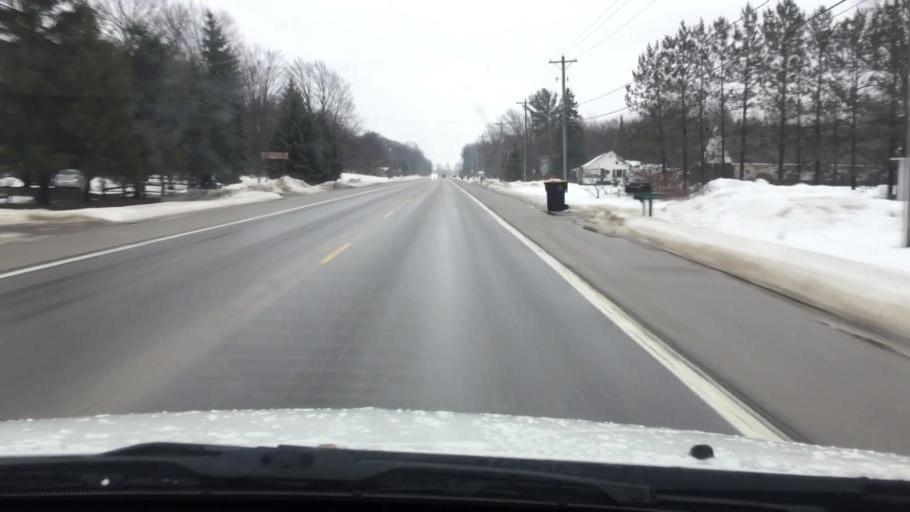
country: US
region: Michigan
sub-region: Charlevoix County
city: Charlevoix
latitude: 45.2915
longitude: -85.2490
